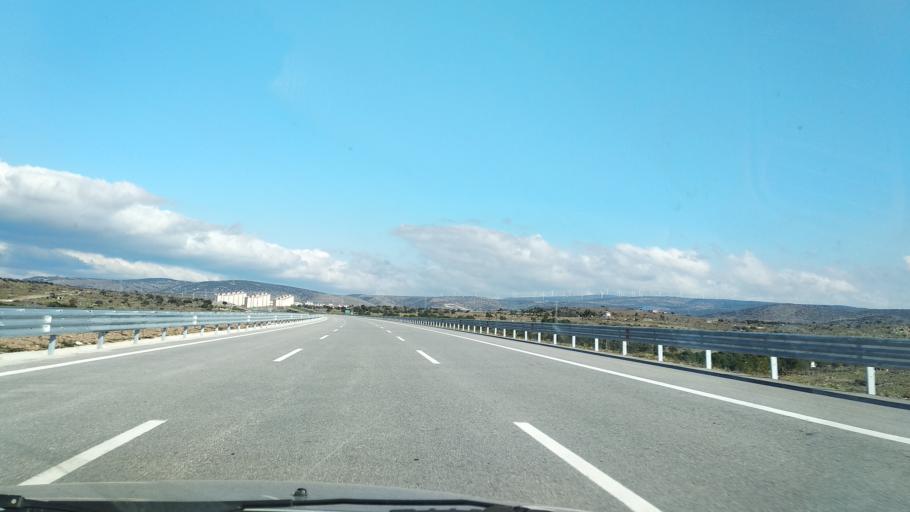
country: TR
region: Izmir
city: Yenisakran
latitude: 38.8653
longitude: 27.0801
